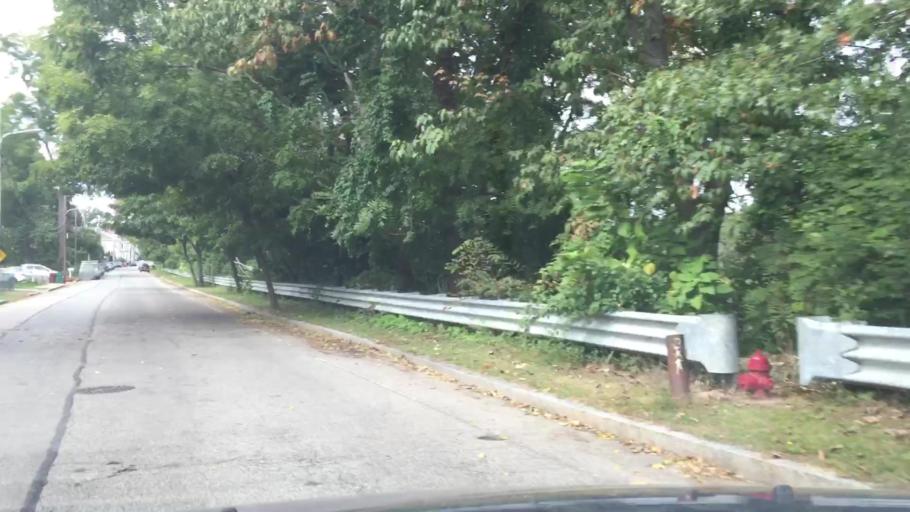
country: US
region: Massachusetts
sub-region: Middlesex County
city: Lowell
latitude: 42.6438
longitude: -71.2940
